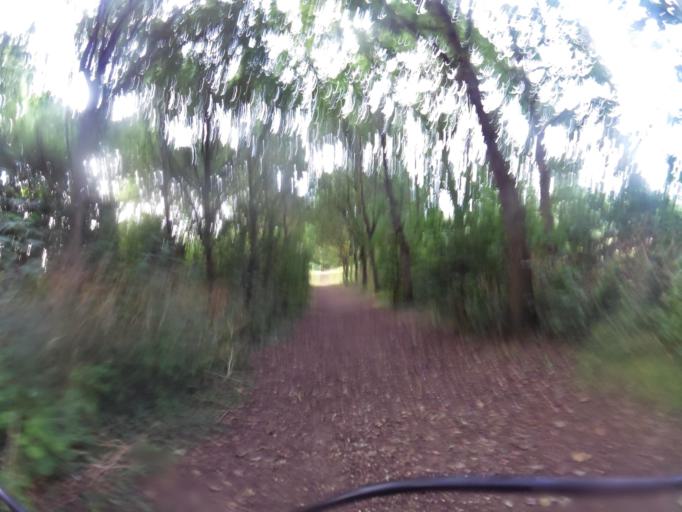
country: GB
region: England
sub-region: Suffolk
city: Bramford
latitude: 52.0359
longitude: 1.1072
